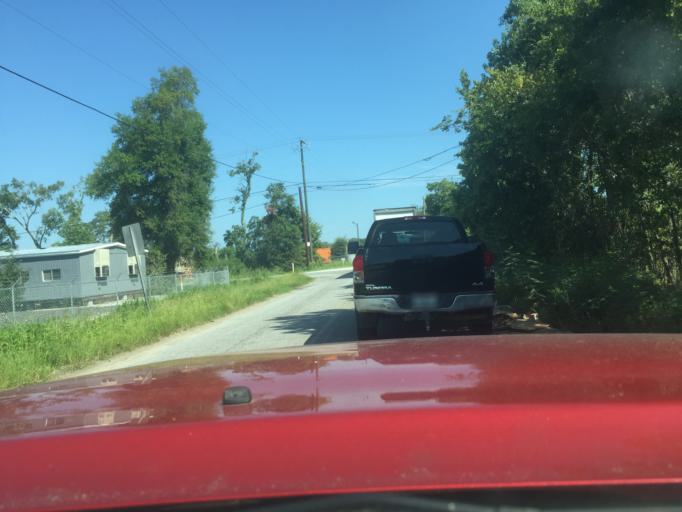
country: US
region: Georgia
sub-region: Chatham County
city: Garden City
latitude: 32.0786
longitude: -81.1458
